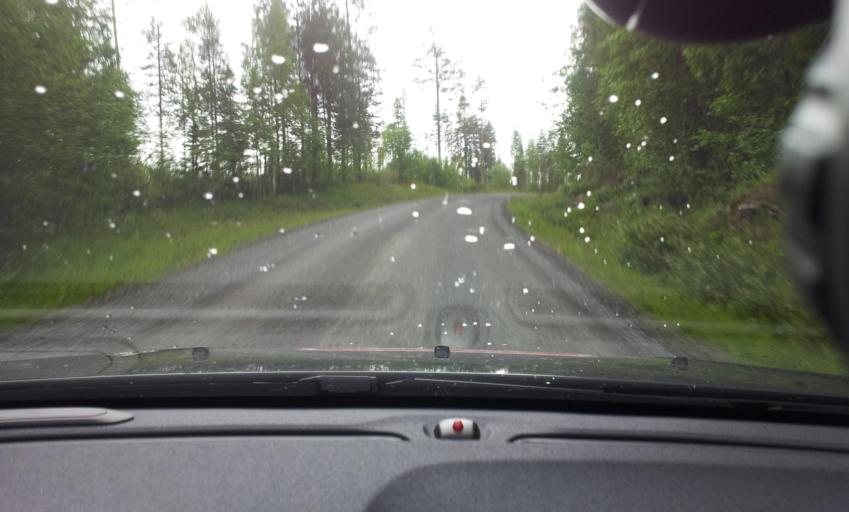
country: SE
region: Jaemtland
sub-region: OEstersunds Kommun
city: Brunflo
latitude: 63.1210
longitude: 15.0914
